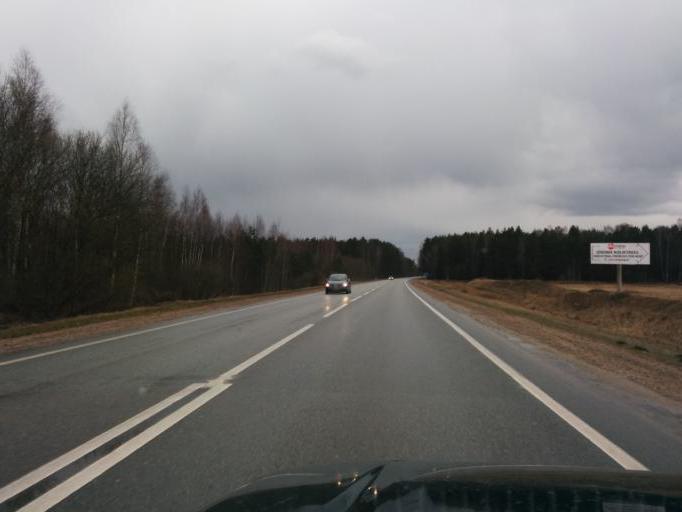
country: LV
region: Marupe
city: Marupe
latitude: 56.8401
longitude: 24.0256
